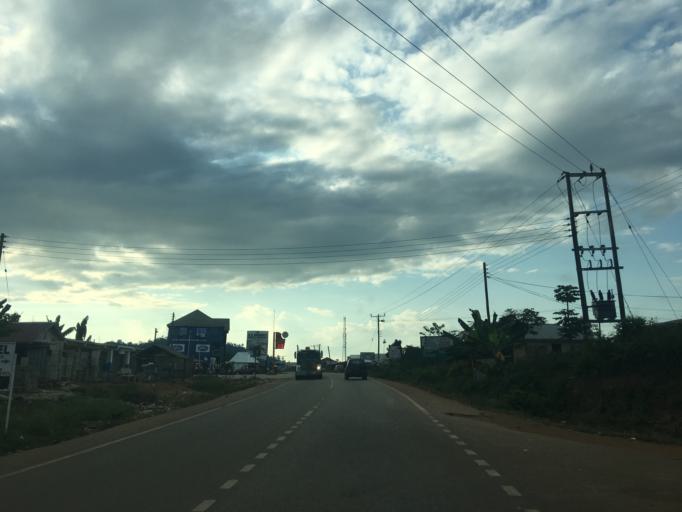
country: GH
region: Western
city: Bibiani
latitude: 6.4387
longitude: -2.3092
